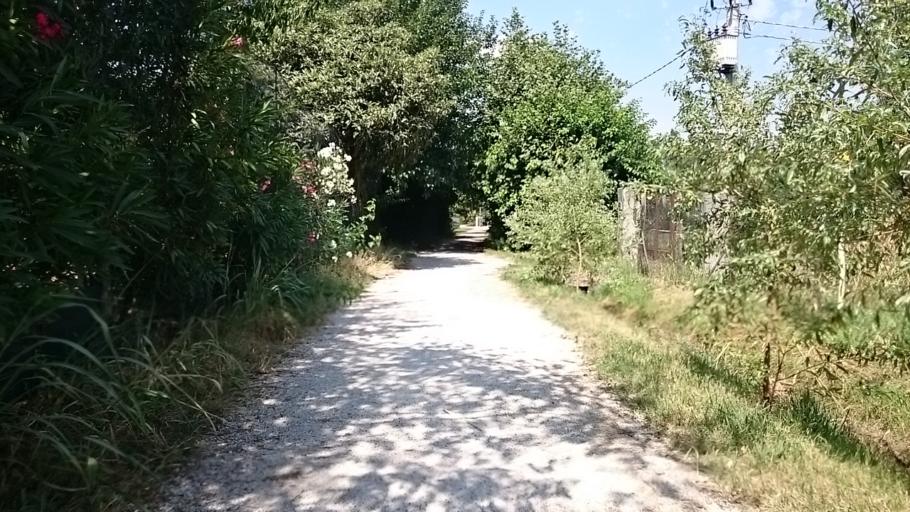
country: IT
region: Veneto
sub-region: Provincia di Vicenza
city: Rosa
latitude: 45.7187
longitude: 11.7364
